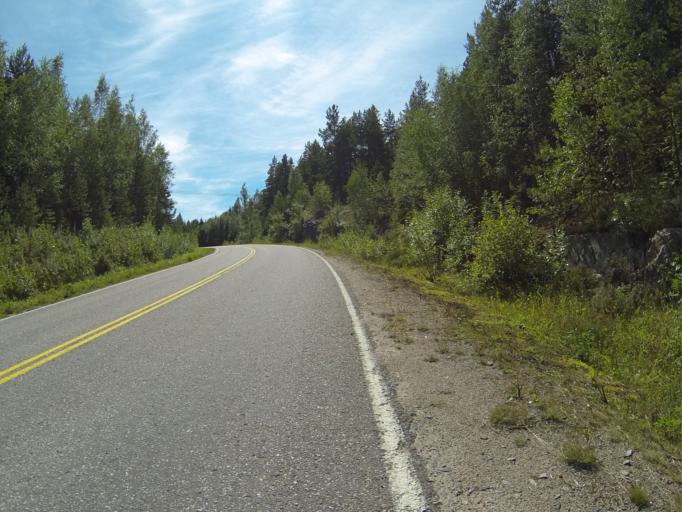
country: FI
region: Varsinais-Suomi
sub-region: Salo
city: Saerkisalo
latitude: 60.2675
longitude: 22.9723
